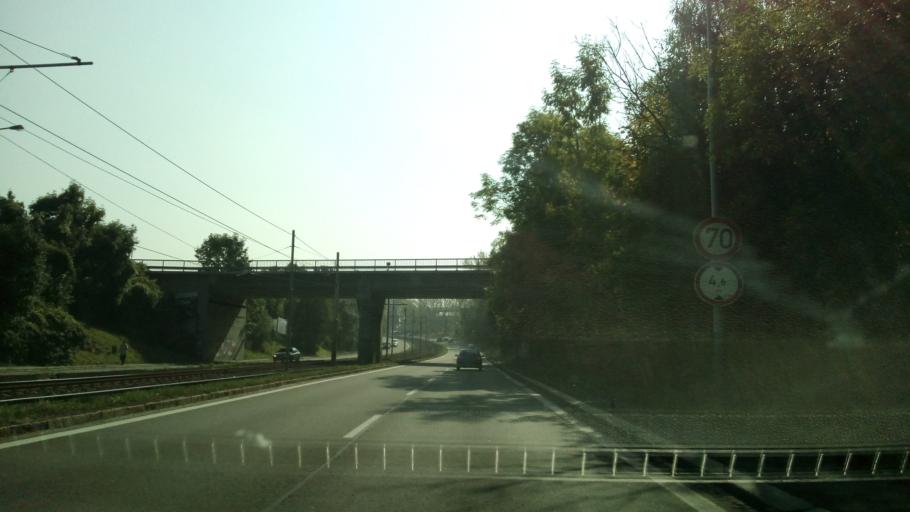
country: CZ
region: Moravskoslezsky
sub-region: Okres Ostrava-Mesto
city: Ostrava
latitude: 49.8191
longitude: 18.2366
